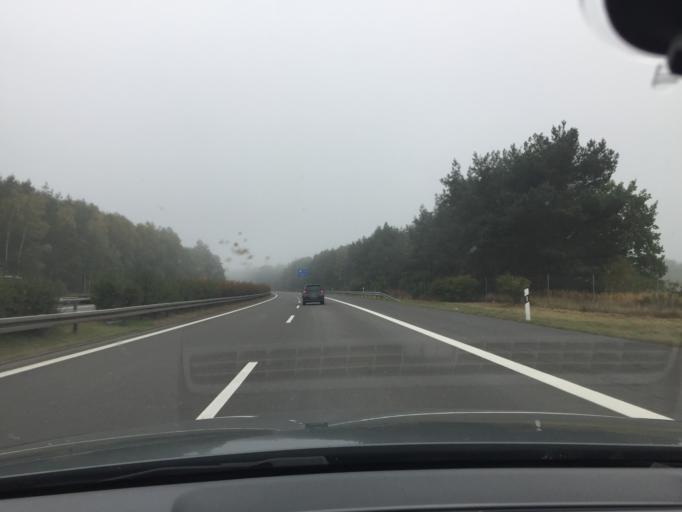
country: DE
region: Brandenburg
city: Bronkow
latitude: 51.6739
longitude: 13.9010
